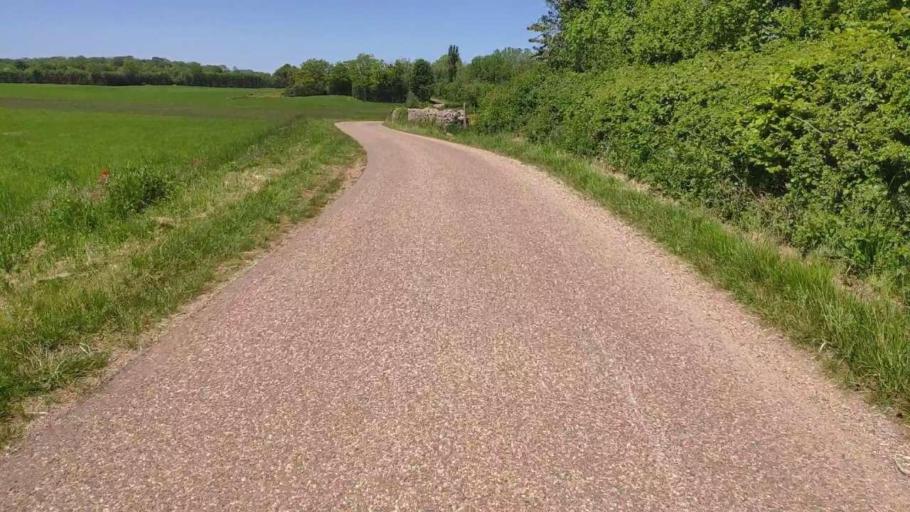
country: FR
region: Franche-Comte
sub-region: Departement du Jura
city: Poligny
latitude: 46.7371
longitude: 5.6903
